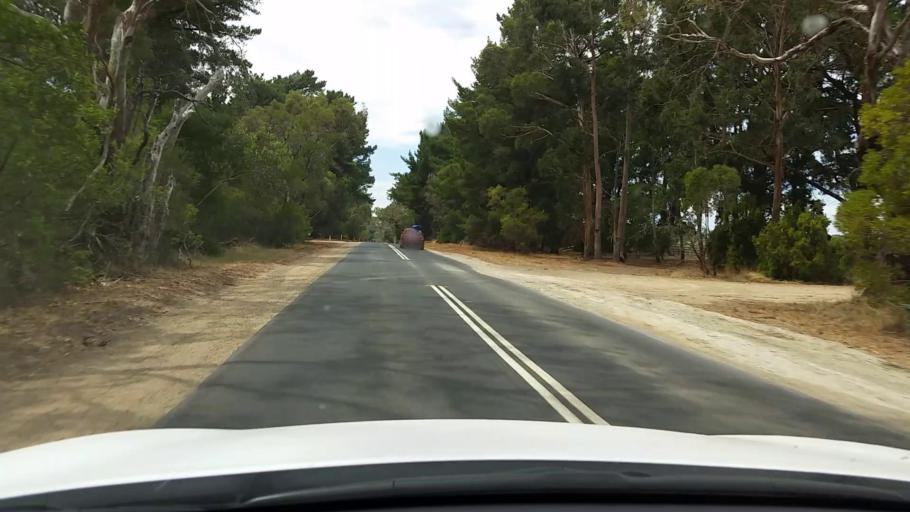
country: AU
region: Victoria
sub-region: Mornington Peninsula
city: Mount Martha
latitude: -38.2923
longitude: 145.0524
